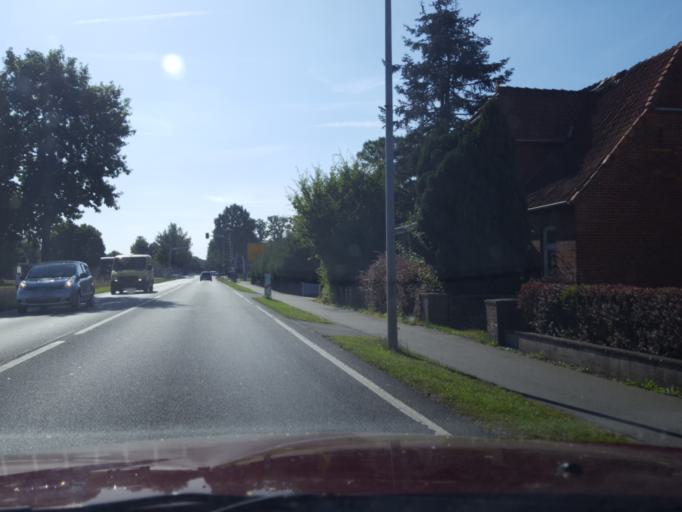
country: DE
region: Lower Saxony
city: Eystrup
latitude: 52.8050
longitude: 9.2058
